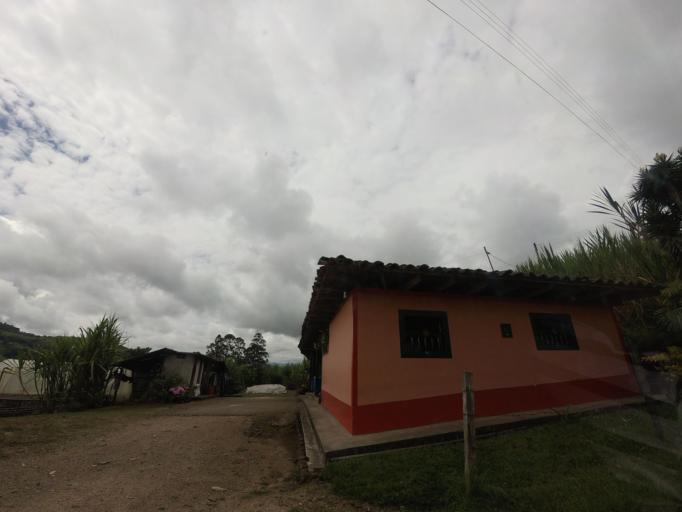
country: CO
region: Huila
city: San Agustin
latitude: 1.9324
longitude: -76.2991
